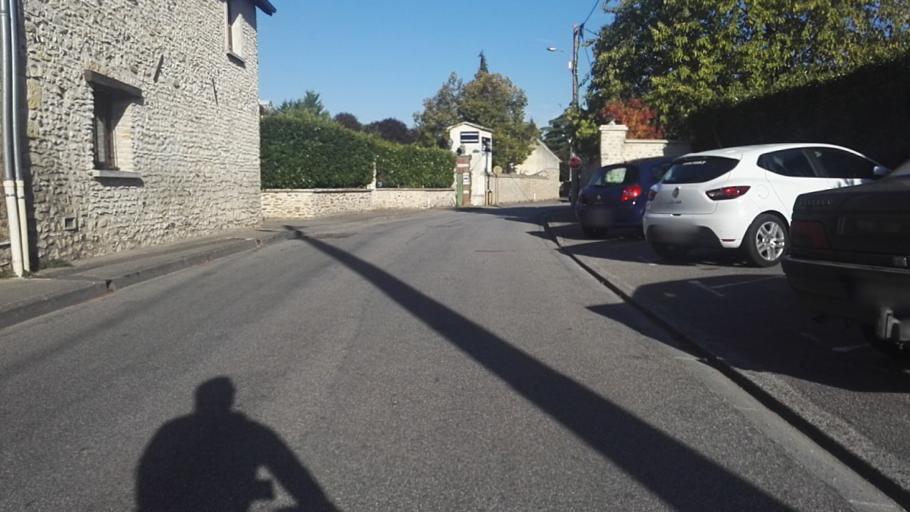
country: FR
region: Haute-Normandie
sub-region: Departement de l'Eure
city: Menilles
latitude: 49.0310
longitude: 1.3632
